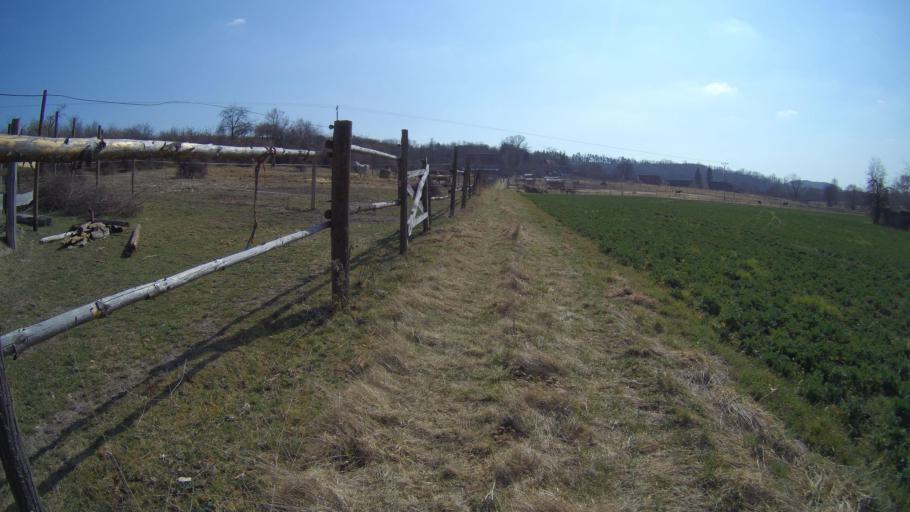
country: CZ
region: Ustecky
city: Zatec
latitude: 50.2939
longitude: 13.5766
